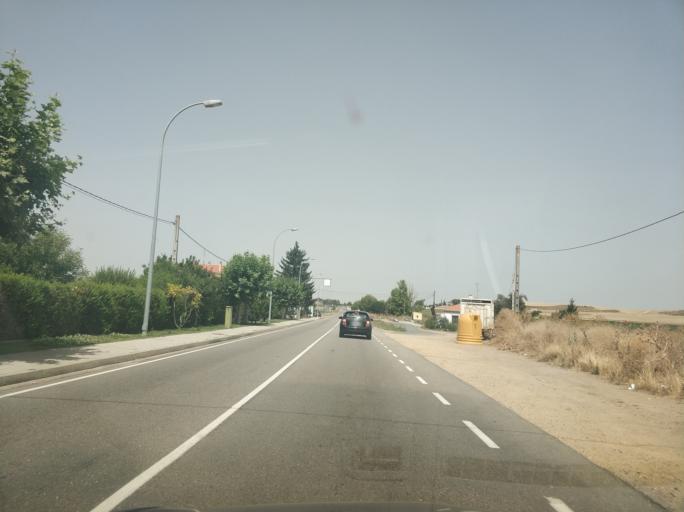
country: ES
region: Castille and Leon
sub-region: Provincia de Salamanca
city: Villamayor
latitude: 41.0004
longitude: -5.6974
